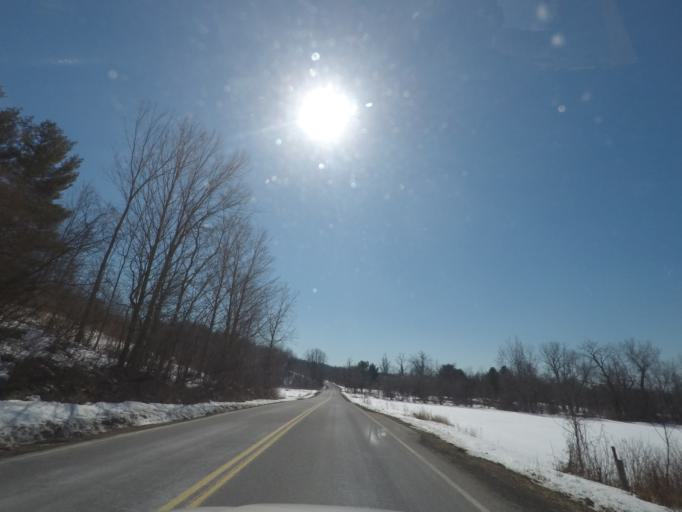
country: US
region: New York
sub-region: Saratoga County
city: Stillwater
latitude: 42.9591
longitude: -73.6231
